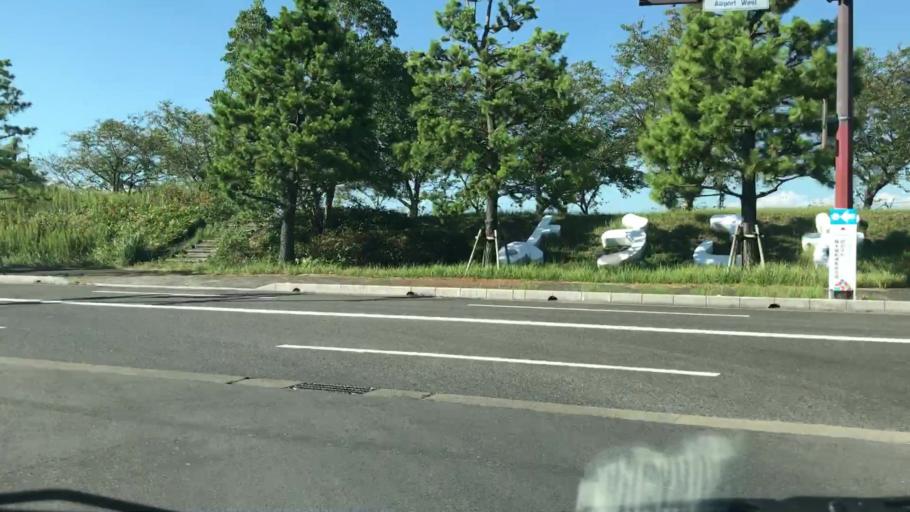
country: JP
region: Saga Prefecture
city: Okawa
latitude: 33.1551
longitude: 130.3020
